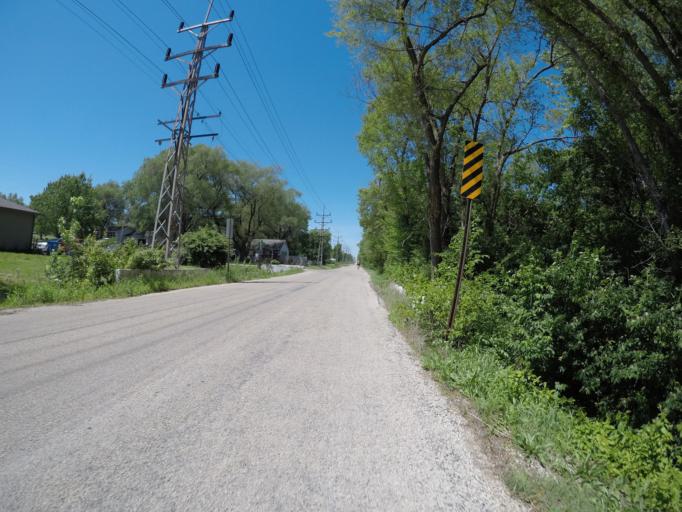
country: US
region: Kansas
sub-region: Shawnee County
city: Topeka
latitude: 39.0517
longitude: -95.6105
